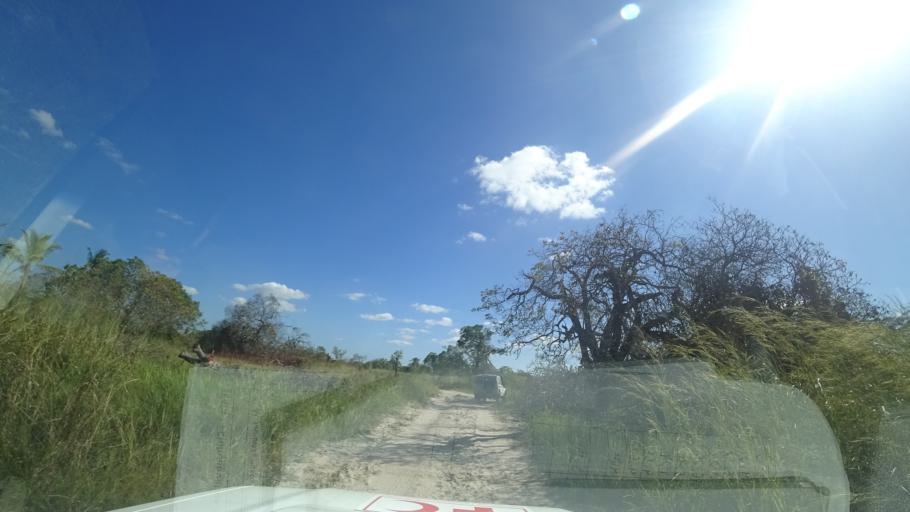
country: MZ
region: Sofala
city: Dondo
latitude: -19.4822
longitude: 34.6213
